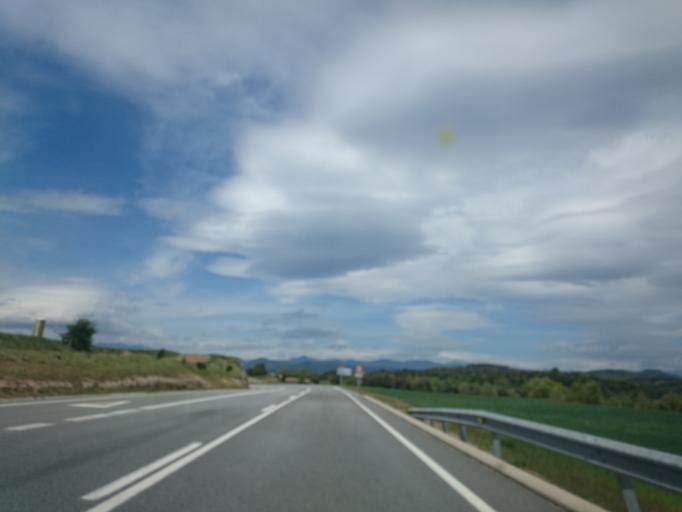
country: ES
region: Catalonia
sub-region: Provincia de Barcelona
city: Prats de Llucanes
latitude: 42.0232
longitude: 2.0252
